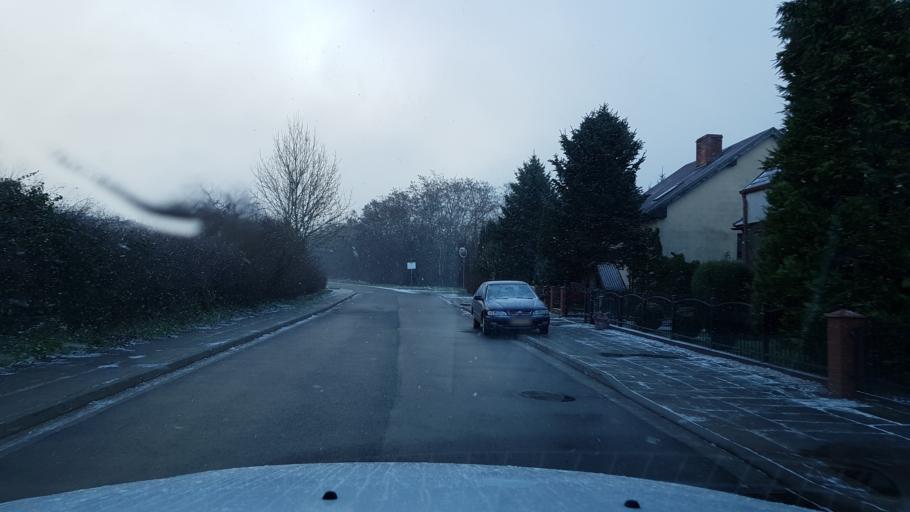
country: PL
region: West Pomeranian Voivodeship
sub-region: Powiat gryficki
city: Trzebiatow
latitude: 54.0570
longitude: 15.2863
